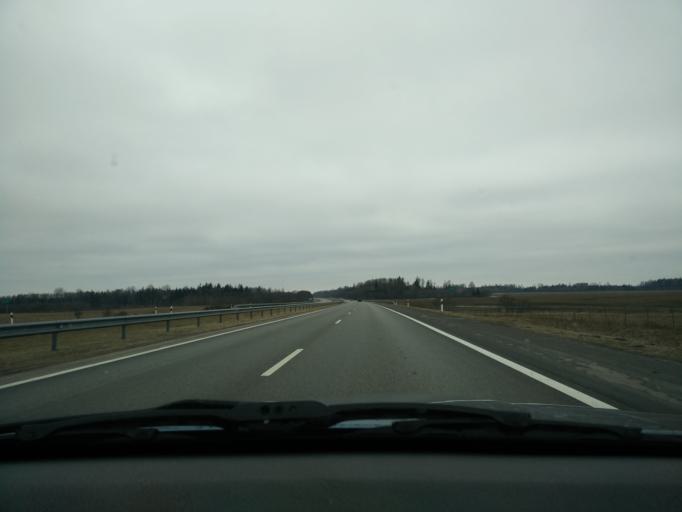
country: LT
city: Rietavas
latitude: 55.6294
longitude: 21.9642
